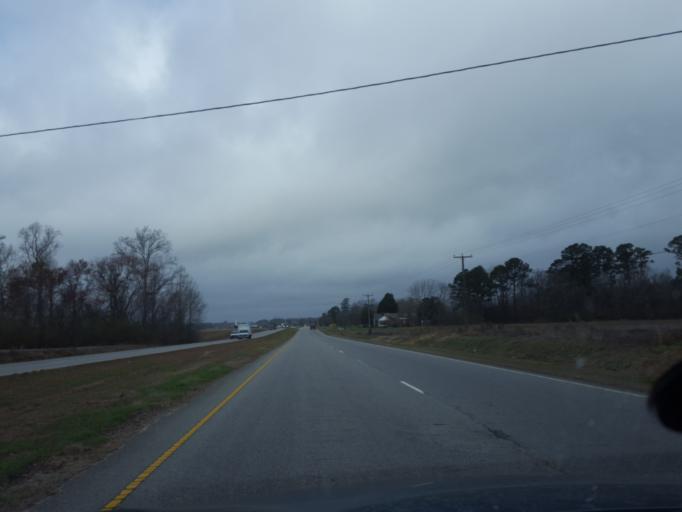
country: US
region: North Carolina
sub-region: Washington County
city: Plymouth
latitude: 35.8319
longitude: -76.7996
